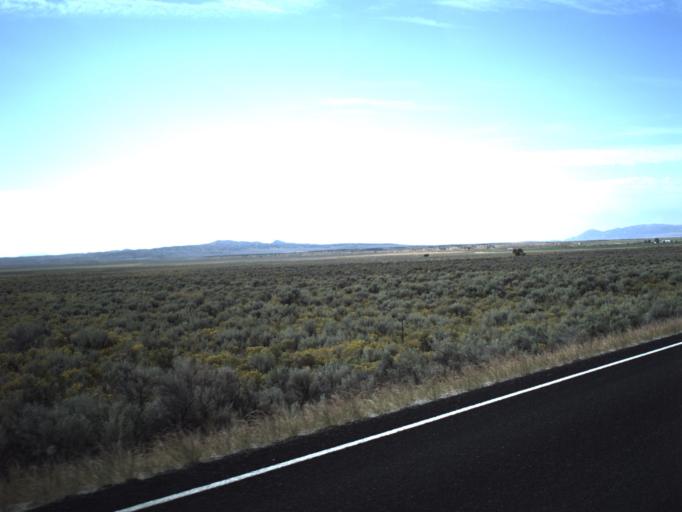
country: US
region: Idaho
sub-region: Cassia County
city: Burley
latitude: 41.7894
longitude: -113.4740
